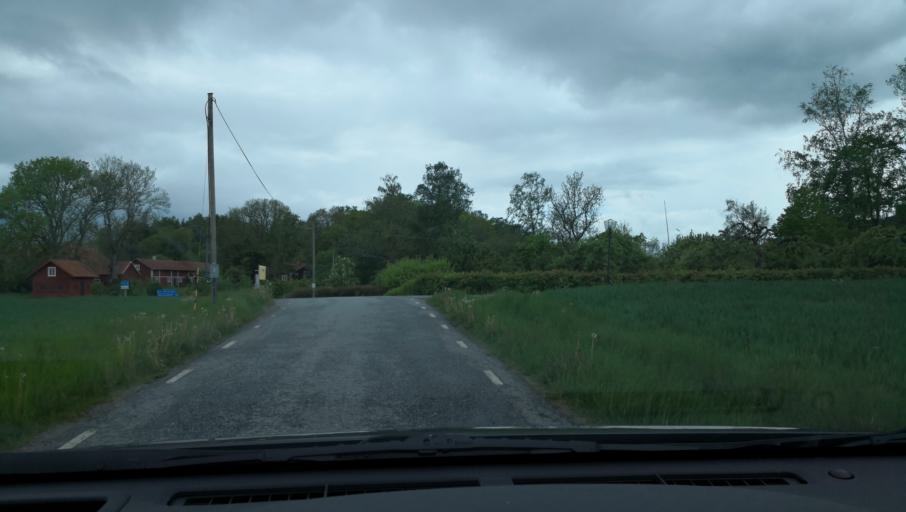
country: SE
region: Uppsala
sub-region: Enkopings Kommun
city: Orsundsbro
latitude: 59.7233
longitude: 17.3463
